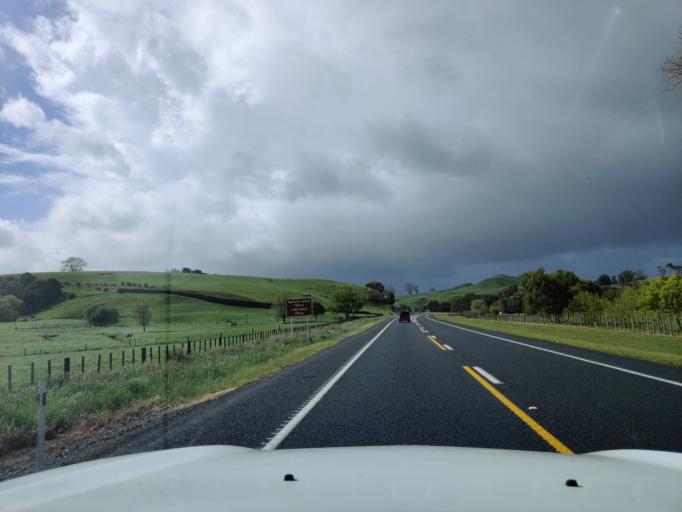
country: NZ
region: Waikato
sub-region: Matamata-Piako District
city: Matamata
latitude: -37.9480
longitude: 175.6732
